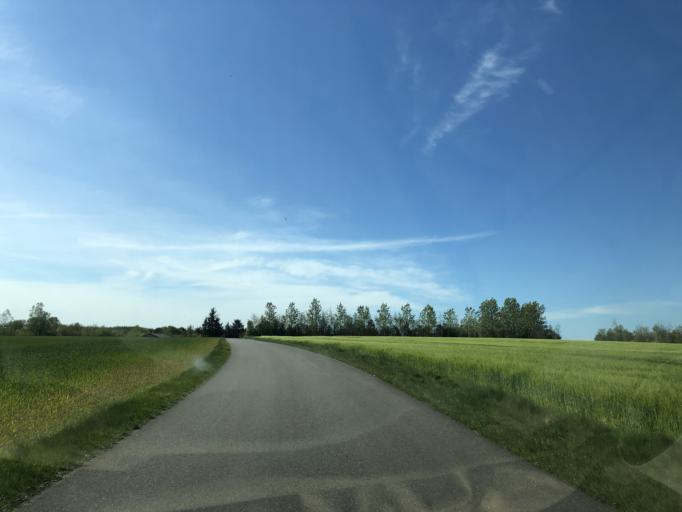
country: DK
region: Central Jutland
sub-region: Ringkobing-Skjern Kommune
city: Videbaek
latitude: 56.1981
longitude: 8.5119
